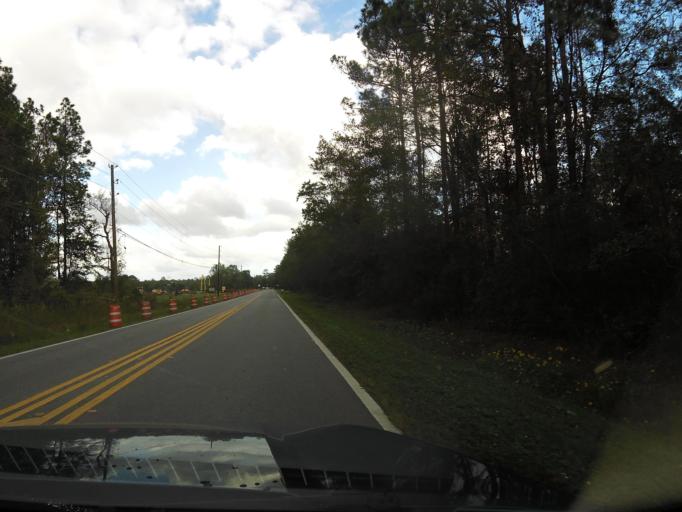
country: US
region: Florida
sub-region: Clay County
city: Asbury Lake
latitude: 30.0537
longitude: -81.7567
